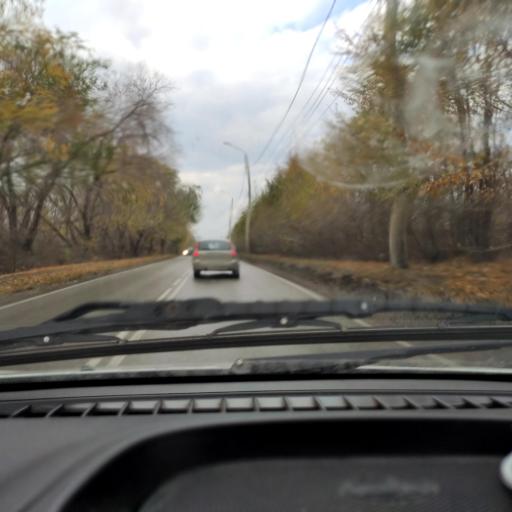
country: RU
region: Samara
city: Zhigulevsk
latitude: 53.4634
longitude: 49.5623
